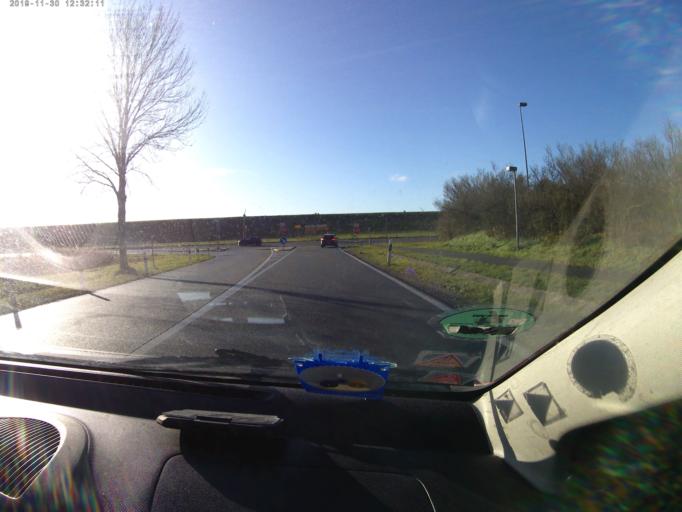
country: DE
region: Lower Saxony
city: Jemgum
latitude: 53.2357
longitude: 7.4110
